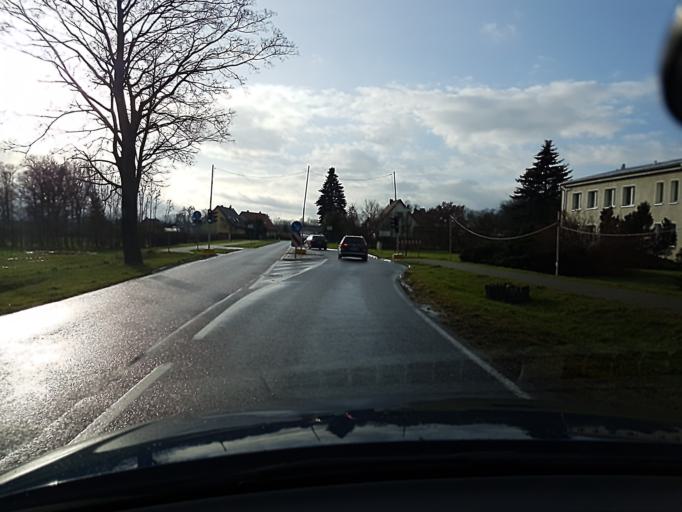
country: DE
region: Mecklenburg-Vorpommern
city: Bad Sulze
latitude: 54.0690
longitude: 12.6765
